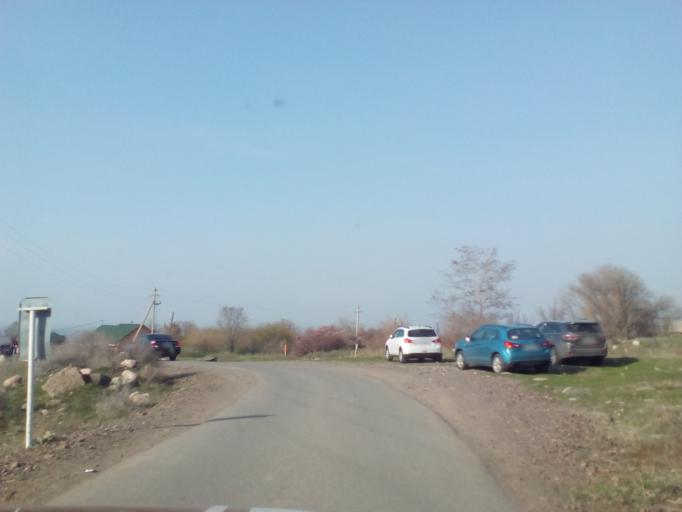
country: KZ
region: Almaty Oblysy
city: Burunday
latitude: 43.1507
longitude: 76.5725
